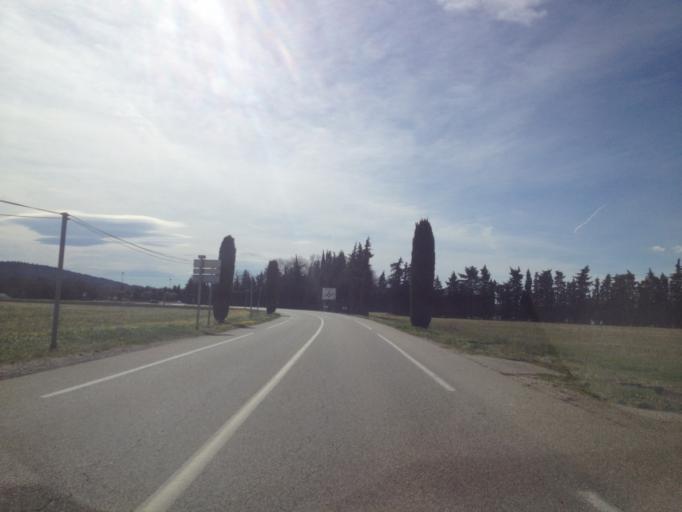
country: FR
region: Provence-Alpes-Cote d'Azur
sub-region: Departement du Vaucluse
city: Violes
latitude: 44.1731
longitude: 4.9603
